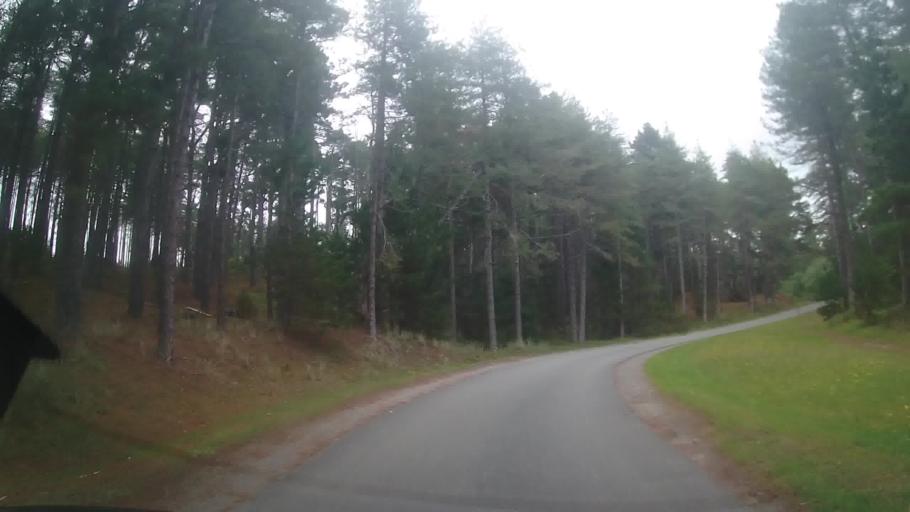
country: GB
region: Wales
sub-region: Gwynedd
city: Caernarfon
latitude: 53.1479
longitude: -4.3848
